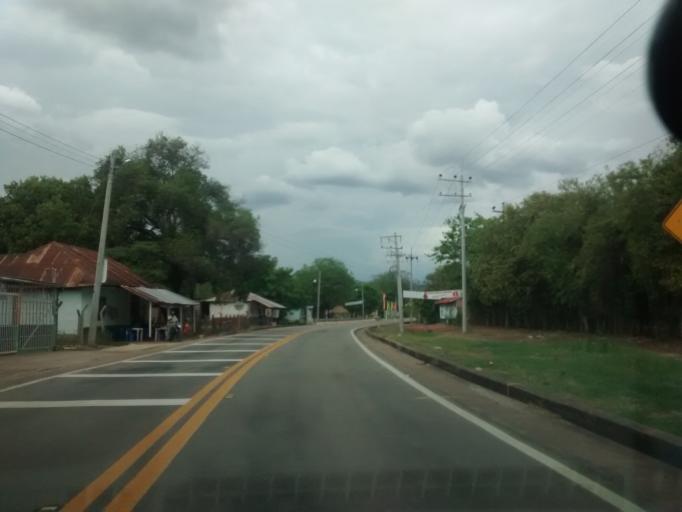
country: CO
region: Cundinamarca
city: Tocaima
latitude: 4.4451
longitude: -74.6666
